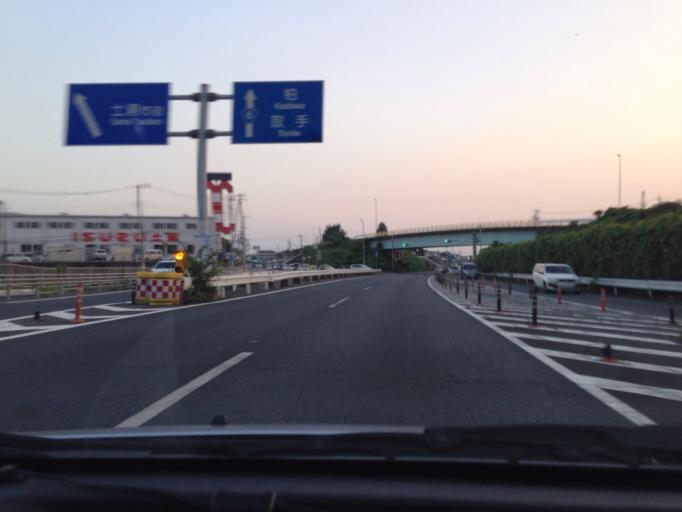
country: JP
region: Ibaraki
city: Naka
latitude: 36.1197
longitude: 140.2110
